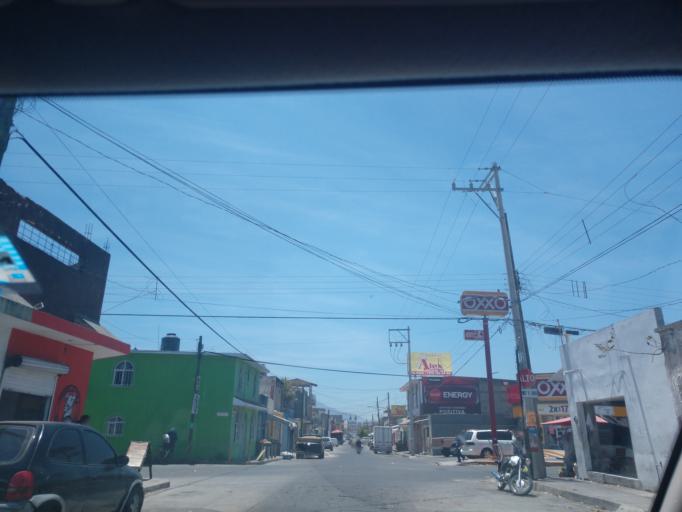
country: MX
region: Nayarit
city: Tepic
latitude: 21.5183
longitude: -104.9021
